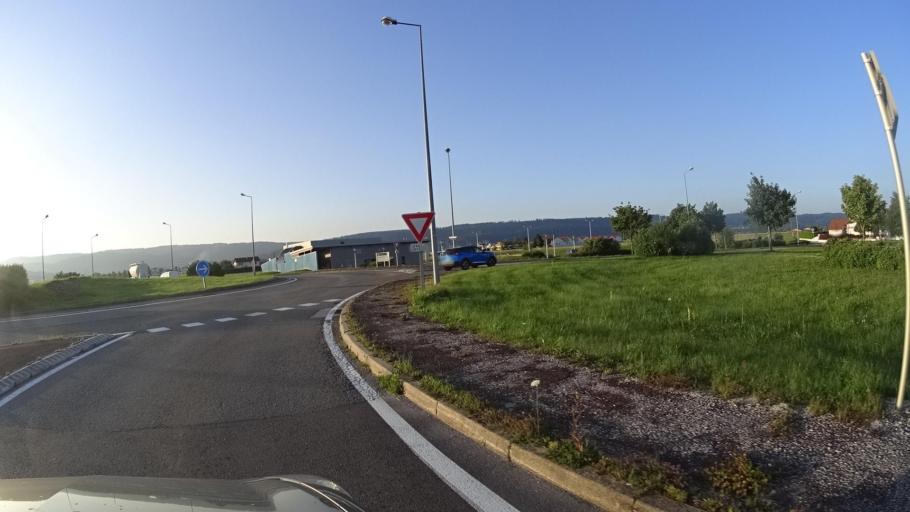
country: FR
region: Franche-Comte
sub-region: Departement du Doubs
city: Doubs
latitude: 46.9121
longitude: 6.3253
